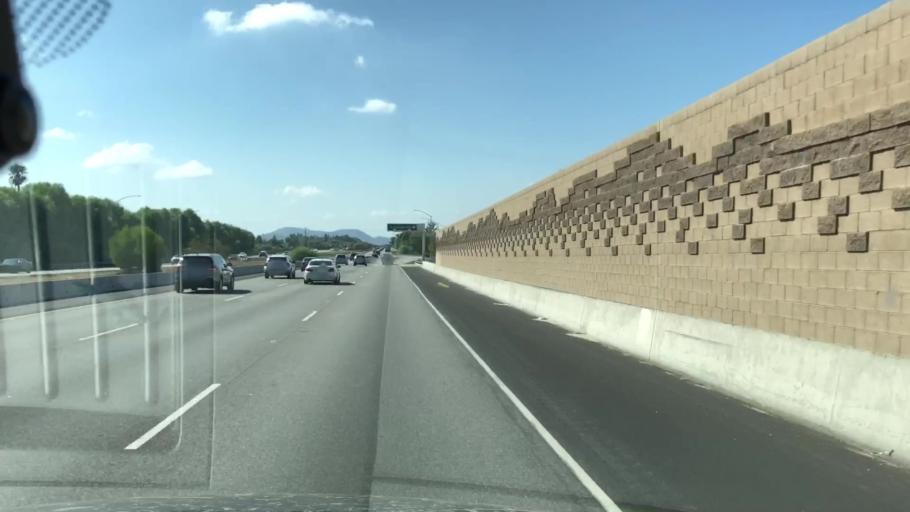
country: US
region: California
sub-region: Ventura County
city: Simi Valley
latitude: 34.2823
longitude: -118.7555
